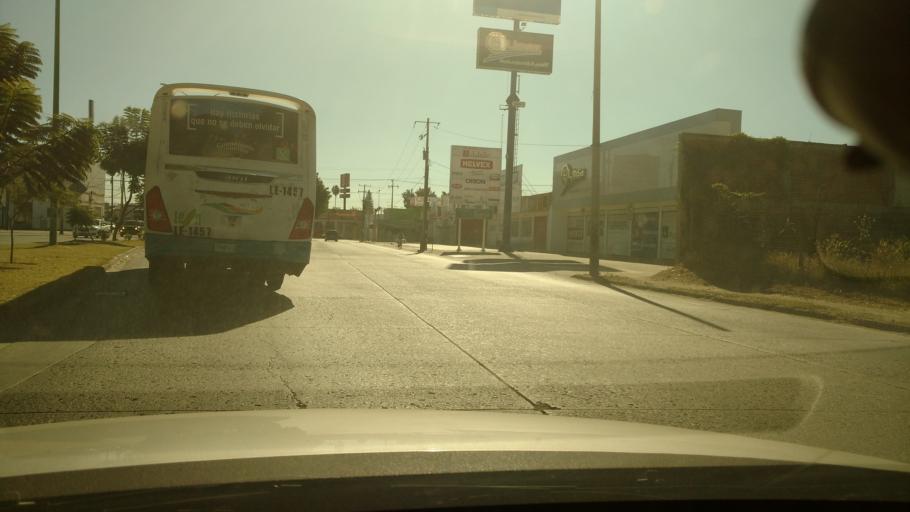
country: MX
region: Guanajuato
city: Leon
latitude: 21.1470
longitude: -101.6736
